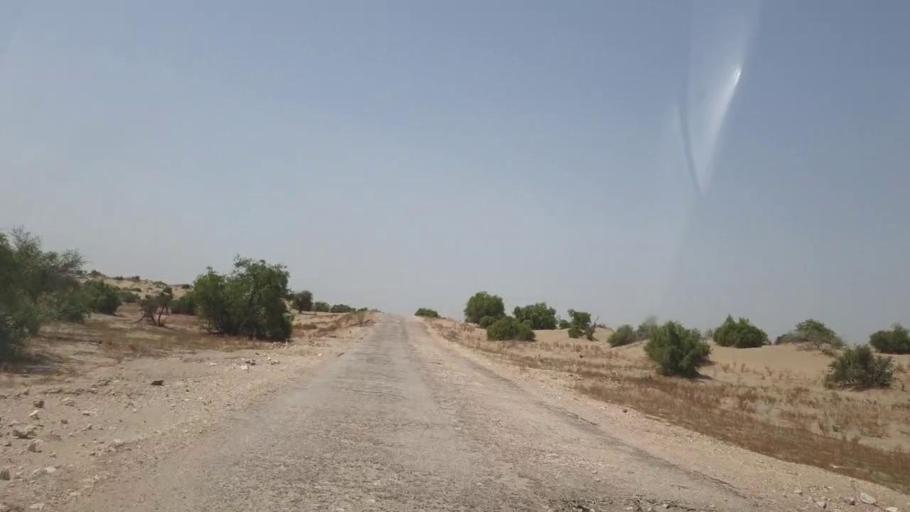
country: PK
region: Sindh
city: Khanpur
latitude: 27.3718
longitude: 69.3186
